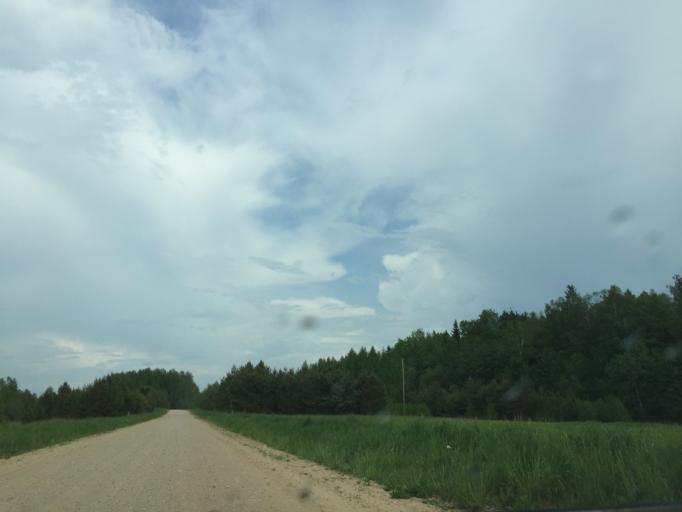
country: LV
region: Livani
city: Livani
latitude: 56.5671
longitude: 26.1460
